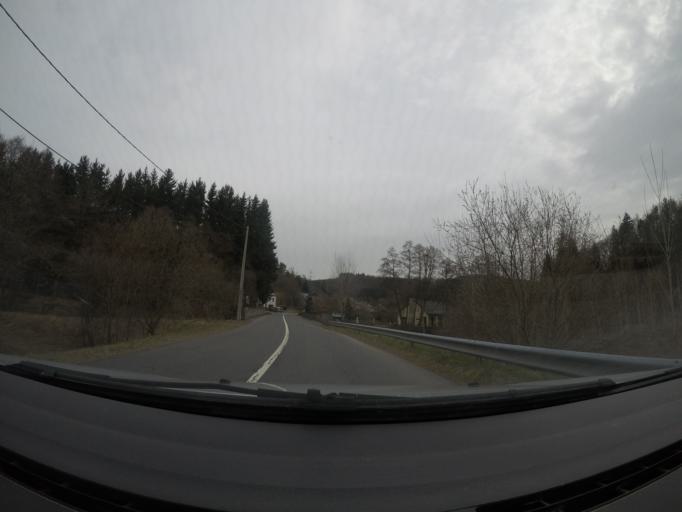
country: BE
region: Wallonia
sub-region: Province du Luxembourg
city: Martelange
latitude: 49.8394
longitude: 5.7200
